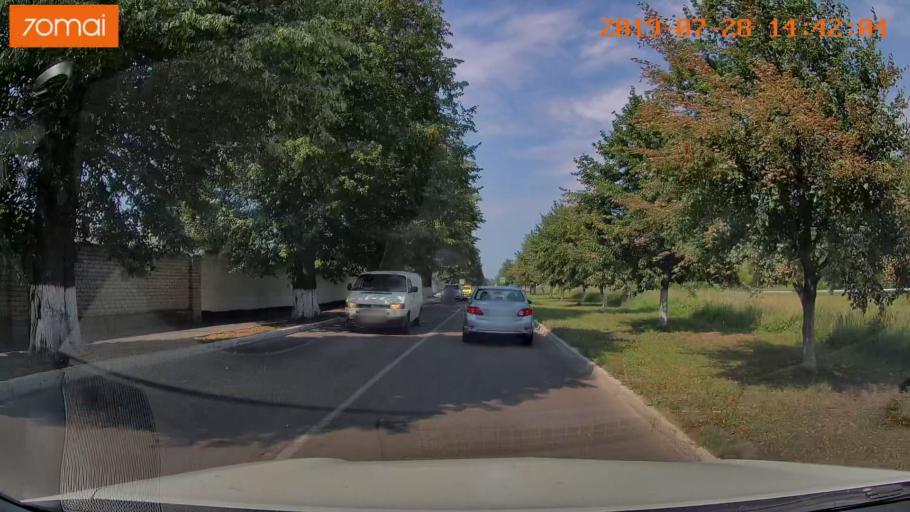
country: RU
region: Kaliningrad
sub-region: Gorod Kaliningrad
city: Yantarnyy
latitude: 54.8579
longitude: 19.9435
